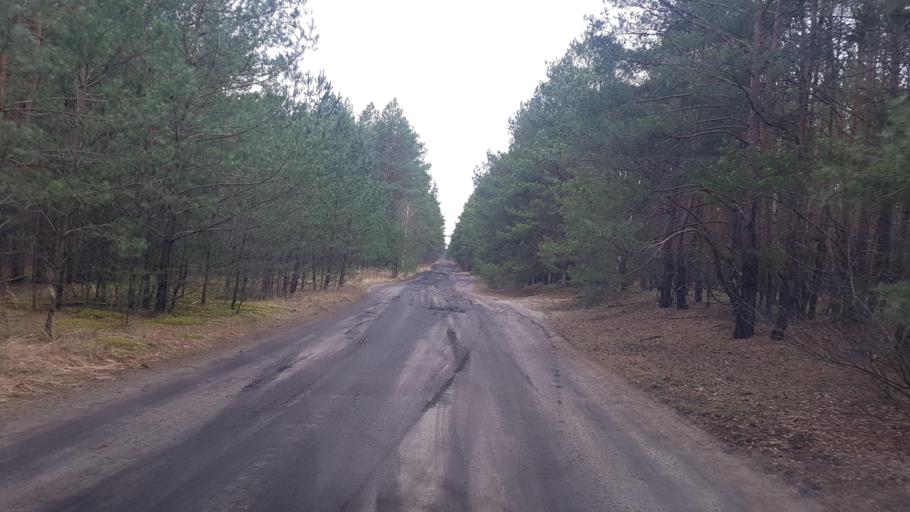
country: DE
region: Brandenburg
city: Halbe
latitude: 52.0637
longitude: 13.6710
